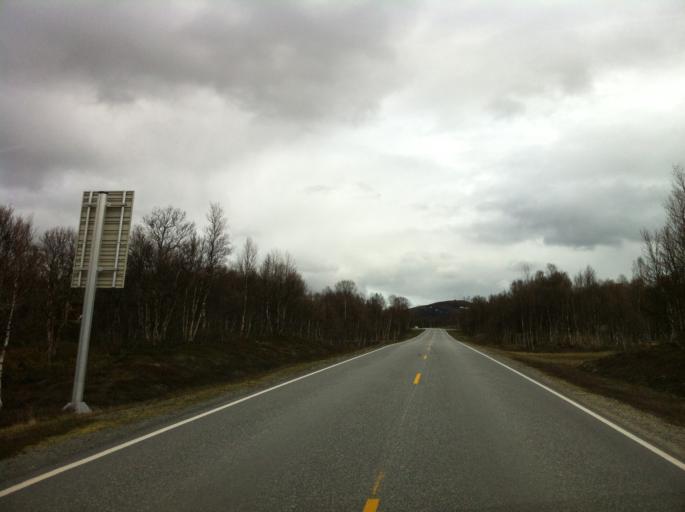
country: NO
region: Sor-Trondelag
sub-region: Roros
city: Roros
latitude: 62.6155
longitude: 11.5919
